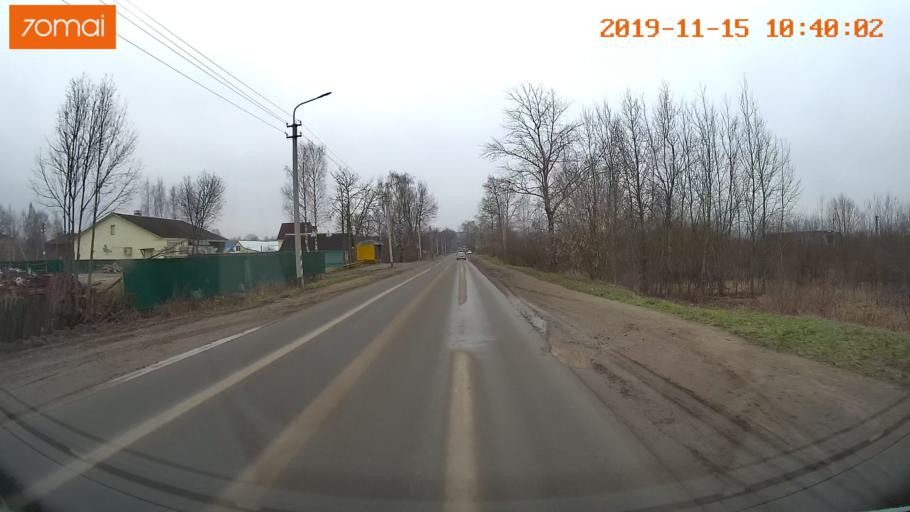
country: RU
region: Vologda
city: Sheksna
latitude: 59.2172
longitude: 38.5104
